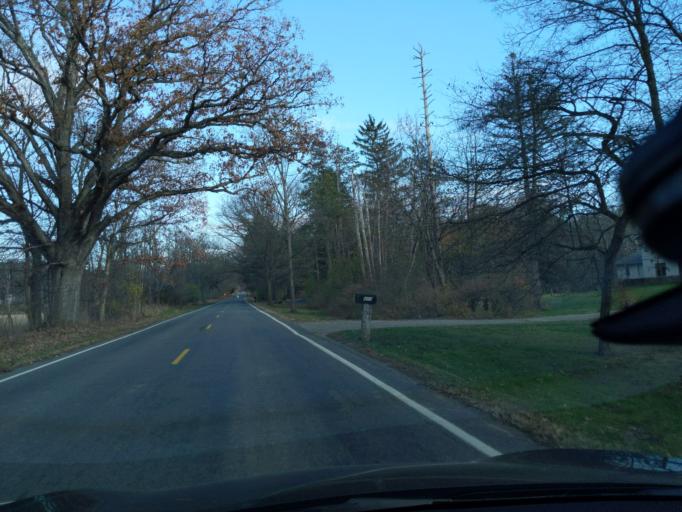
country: US
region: Michigan
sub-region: Ingham County
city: Haslett
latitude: 42.7154
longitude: -84.3481
